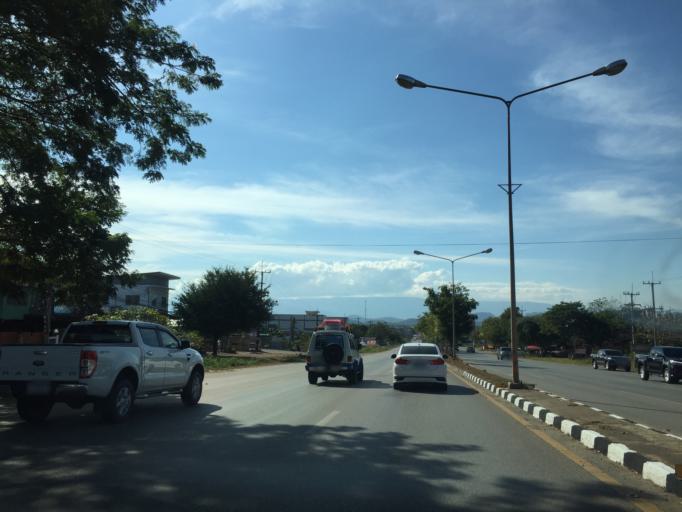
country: TH
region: Loei
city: Wang Saphung
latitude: 17.3015
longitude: 101.7886
